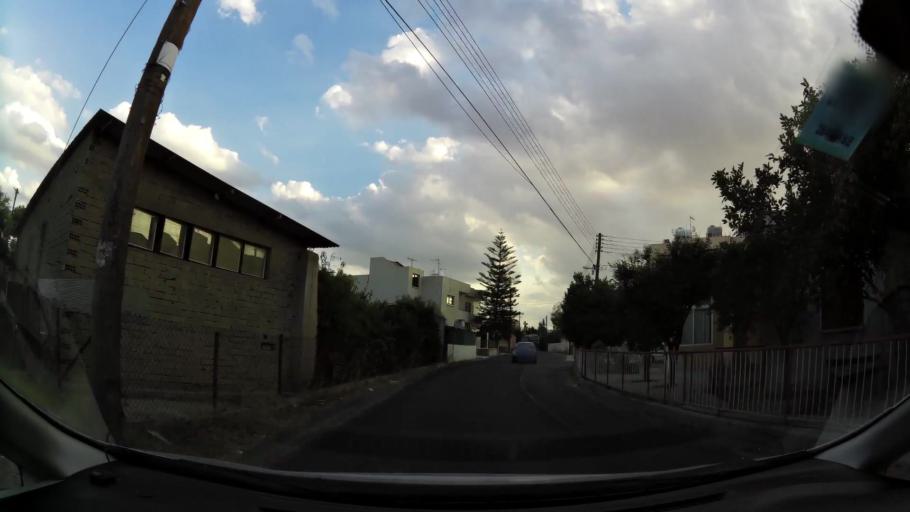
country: CY
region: Lefkosia
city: Tseri
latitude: 35.1185
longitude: 33.3123
